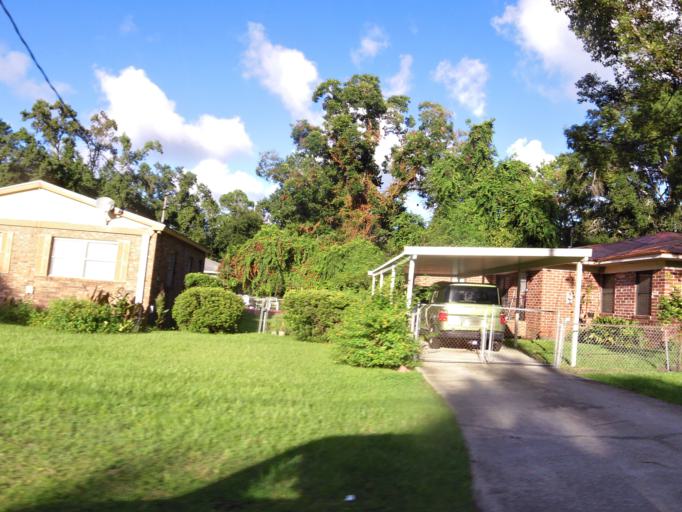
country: US
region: Georgia
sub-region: Glynn County
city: Brunswick
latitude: 31.1793
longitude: -81.4924
